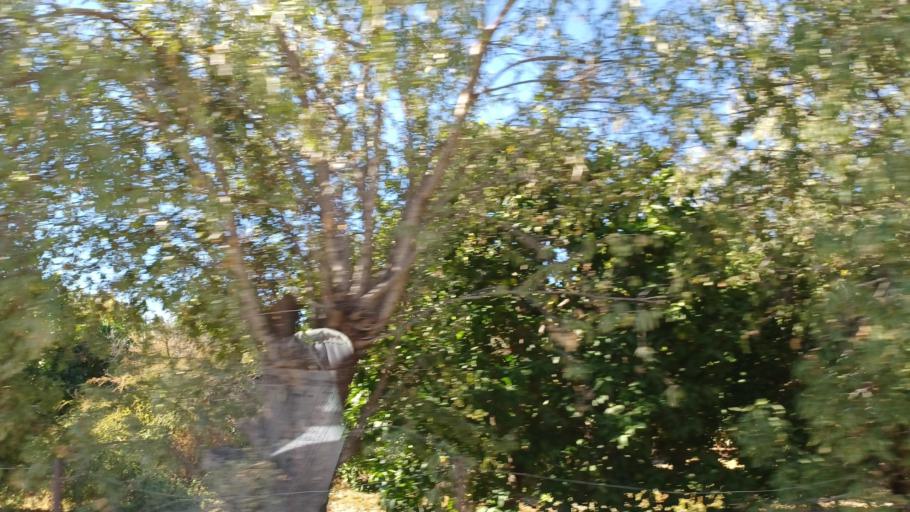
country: CY
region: Pafos
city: Polis
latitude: 35.0258
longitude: 32.4215
